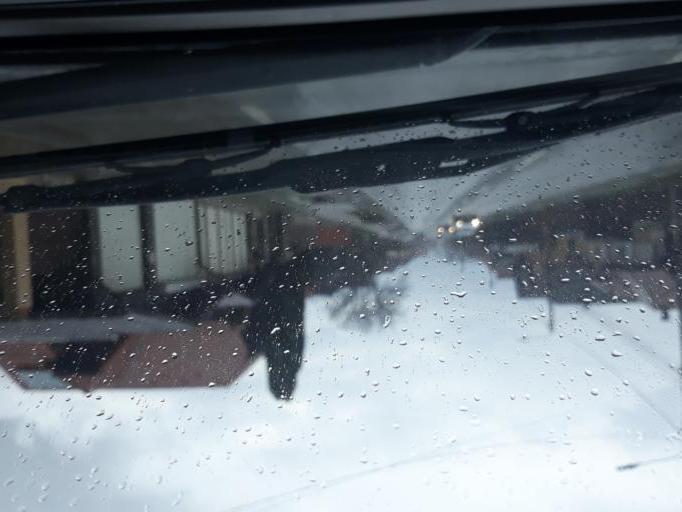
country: RO
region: Harghita
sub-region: Comuna Corund
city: Corund
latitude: 46.4755
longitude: 25.1771
